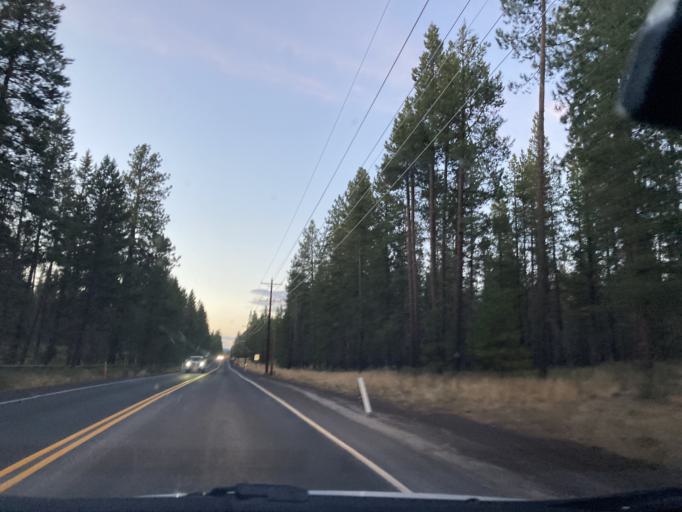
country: US
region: Oregon
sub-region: Deschutes County
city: Three Rivers
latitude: 43.8349
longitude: -121.4420
